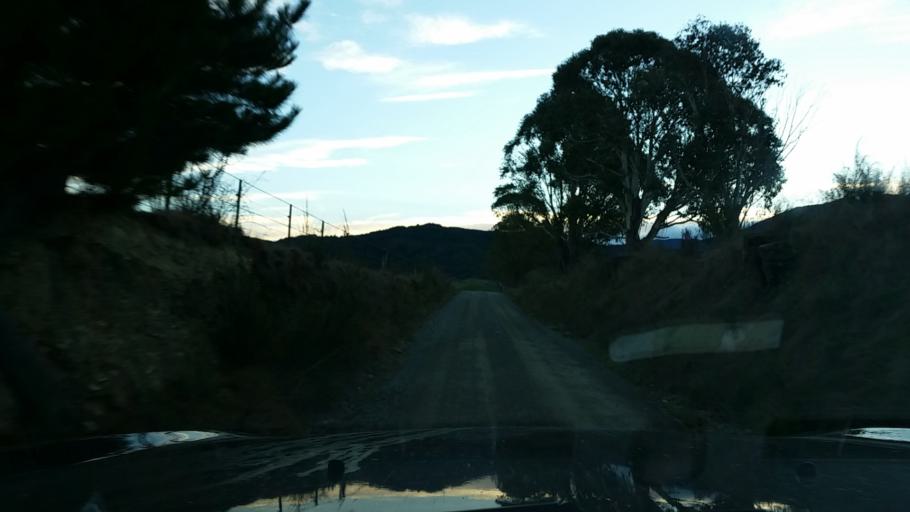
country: NZ
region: Marlborough
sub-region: Marlborough District
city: Blenheim
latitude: -41.5139
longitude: 173.5901
